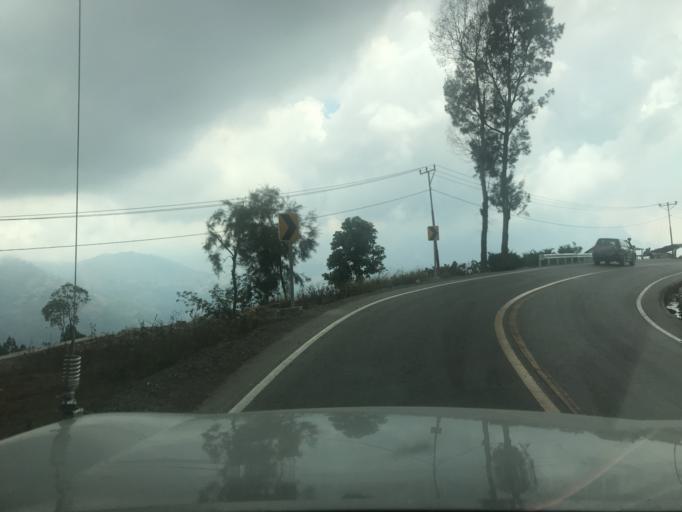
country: TL
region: Manufahi
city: Same
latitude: -8.8892
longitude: 125.5996
